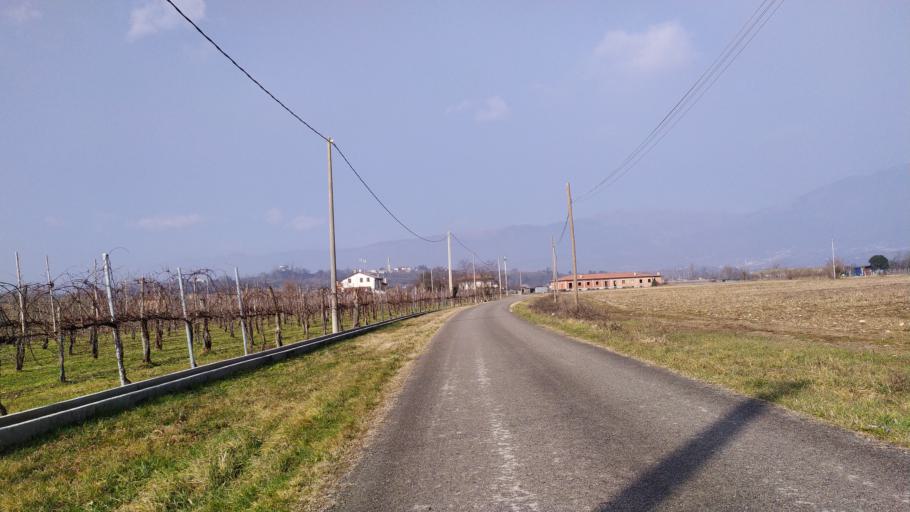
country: IT
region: Veneto
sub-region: Provincia di Treviso
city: San Fior di Sopra
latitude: 45.9439
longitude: 12.3666
